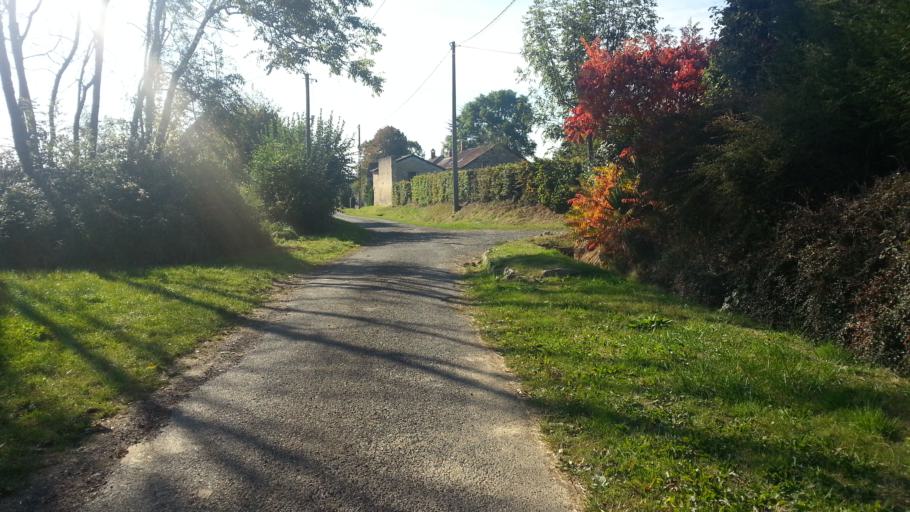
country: FR
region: Ile-de-France
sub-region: Departement de Seine-et-Marne
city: Villiers-Saint-Georges
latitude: 48.7493
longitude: 3.4268
